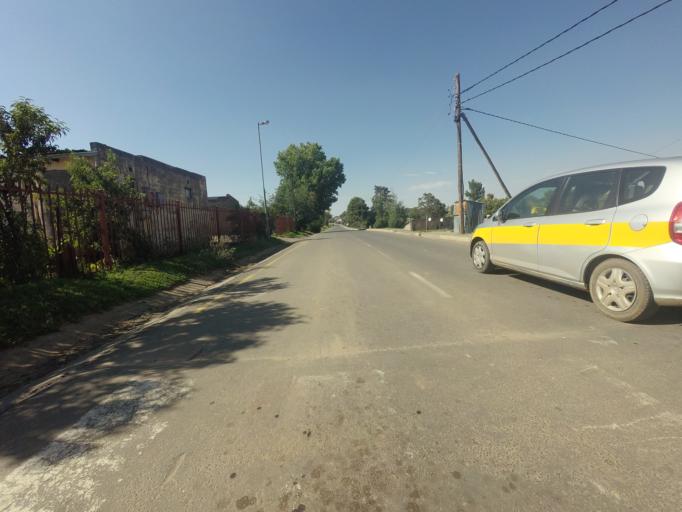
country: LS
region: Berea
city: Teyateyaneng
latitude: -29.1409
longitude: 27.7497
